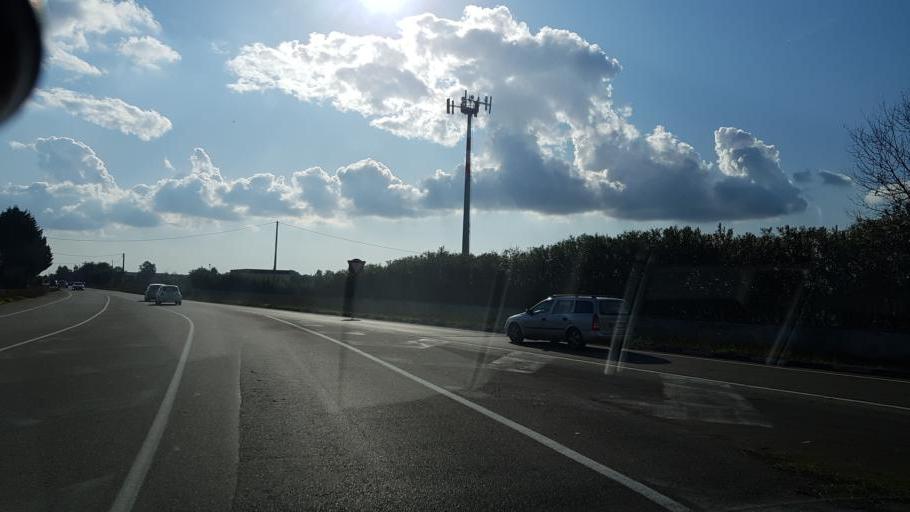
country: IT
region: Apulia
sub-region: Provincia di Lecce
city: Salice Salentino
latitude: 40.3734
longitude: 17.9668
